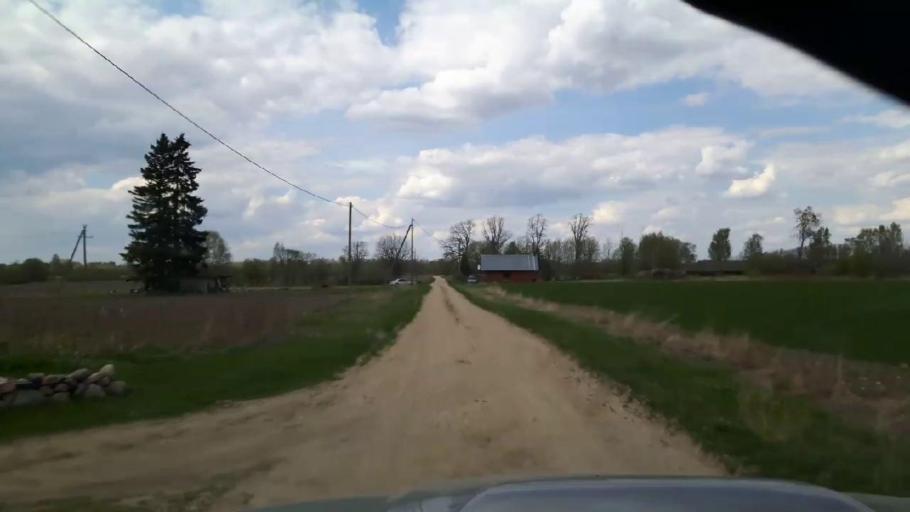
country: EE
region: Paernumaa
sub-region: Sindi linn
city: Sindi
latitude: 58.4149
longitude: 24.7016
